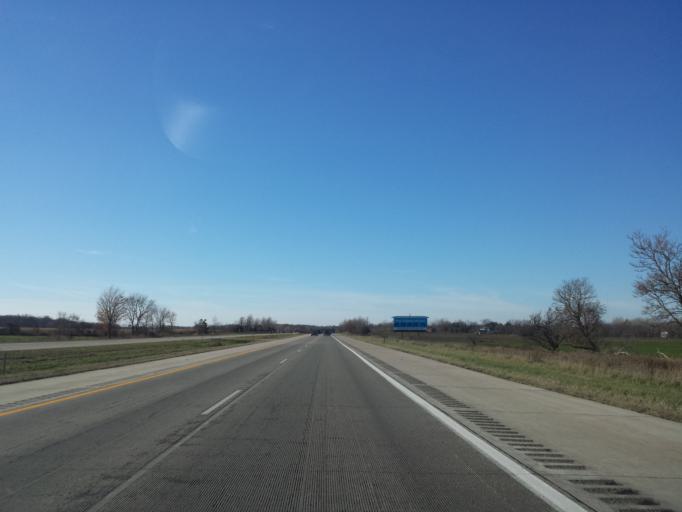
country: US
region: Michigan
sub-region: Ingham County
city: Okemos
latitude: 42.6714
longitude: -84.3655
